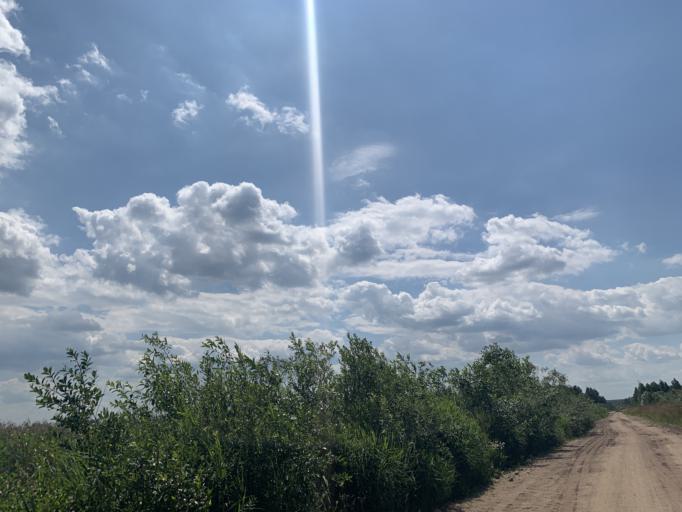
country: BY
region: Minsk
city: Nyasvizh
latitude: 53.2244
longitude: 26.7416
